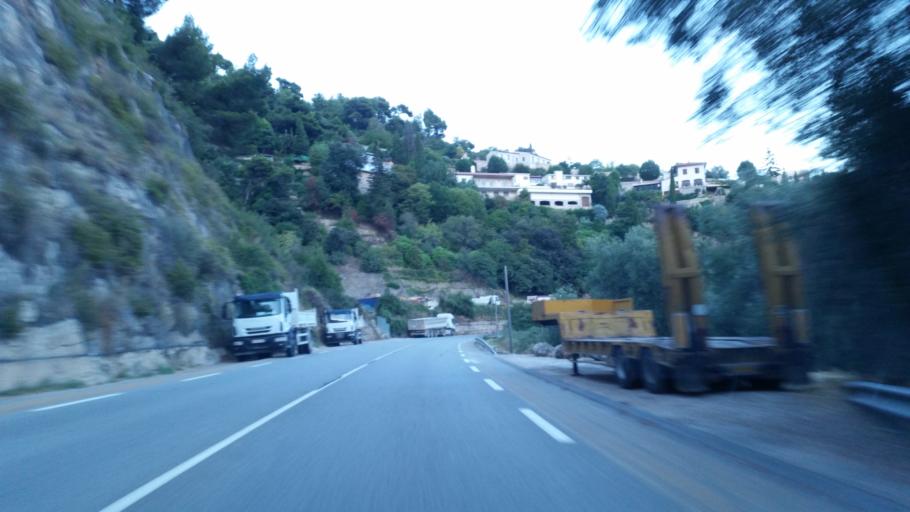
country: MC
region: Commune de Monaco
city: Saint-Roman
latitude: 43.7573
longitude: 7.4360
